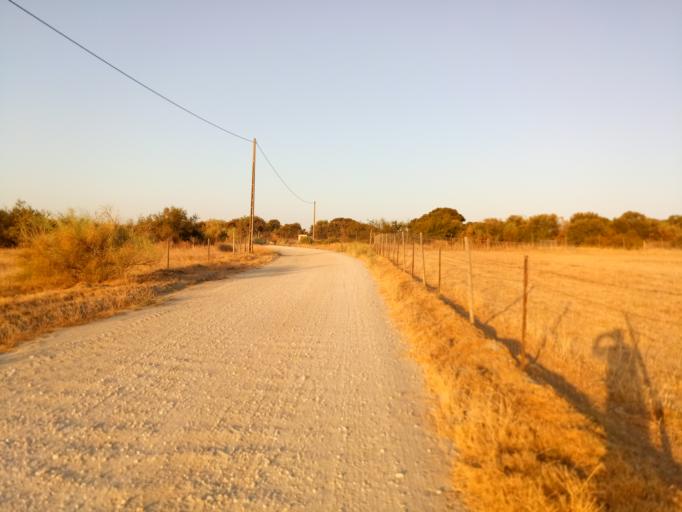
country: PT
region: Evora
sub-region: Reguengos de Monsaraz
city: Reguengos de Monsaraz
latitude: 38.3810
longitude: -7.4538
